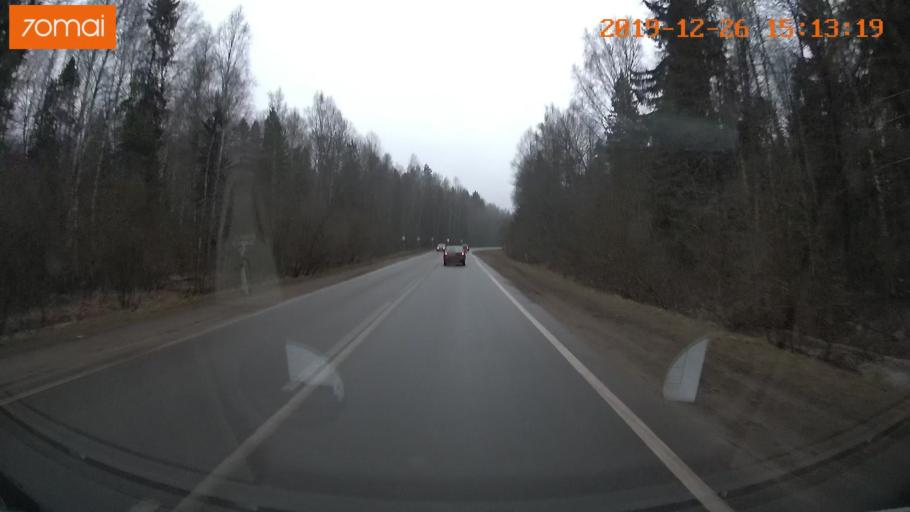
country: RU
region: Jaroslavl
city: Rybinsk
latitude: 58.1184
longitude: 38.8838
